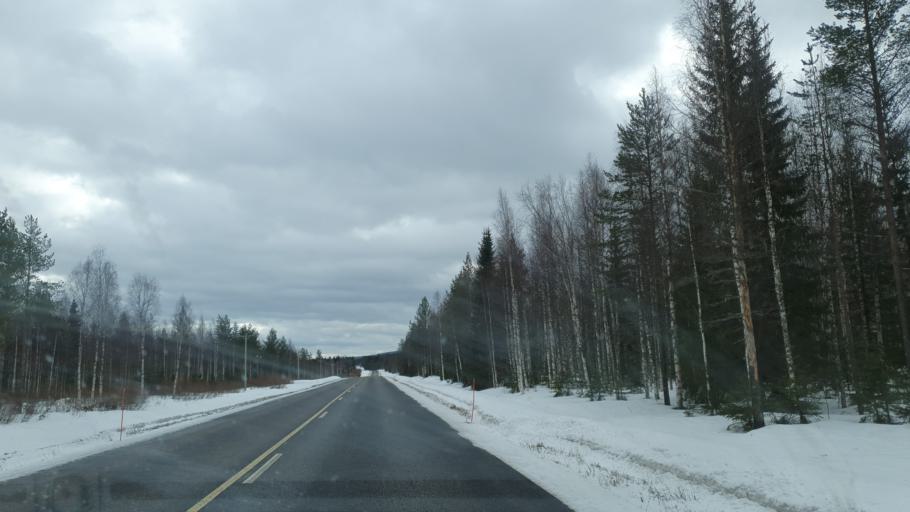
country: FI
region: Kainuu
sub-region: Kehys-Kainuu
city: Puolanka
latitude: 65.2131
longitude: 27.6017
